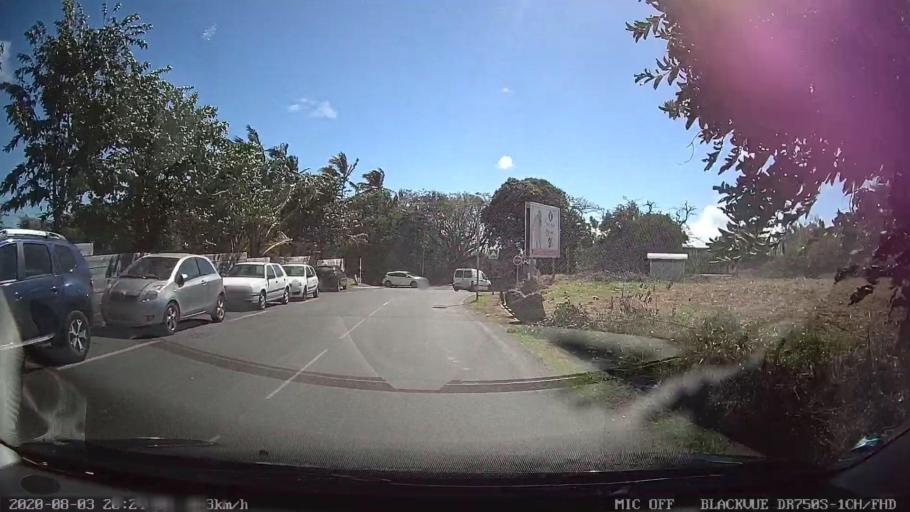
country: RE
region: Reunion
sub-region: Reunion
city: Sainte-Marie
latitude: -20.8954
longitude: 55.5369
